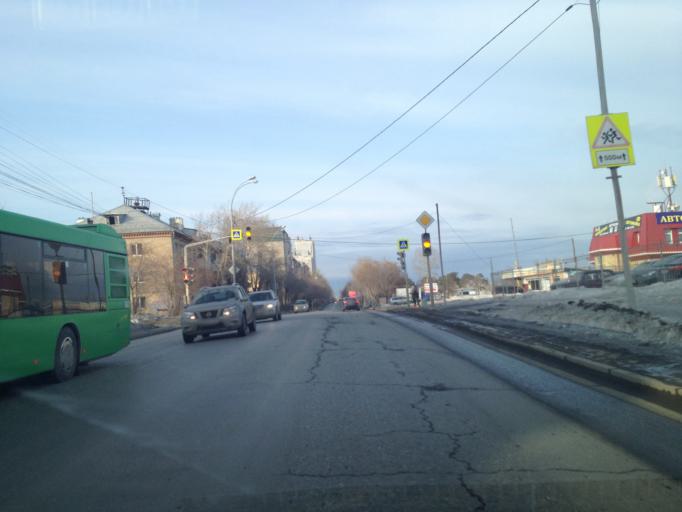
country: RU
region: Sverdlovsk
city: Sovkhoznyy
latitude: 56.7581
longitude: 60.6106
